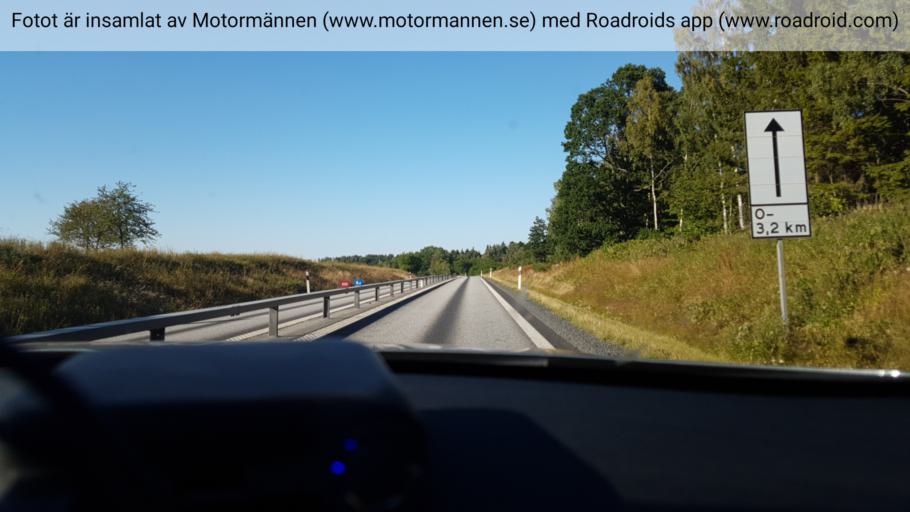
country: SE
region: Joenkoeping
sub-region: Jonkopings Kommun
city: Bankeryd
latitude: 57.8379
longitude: 14.1044
